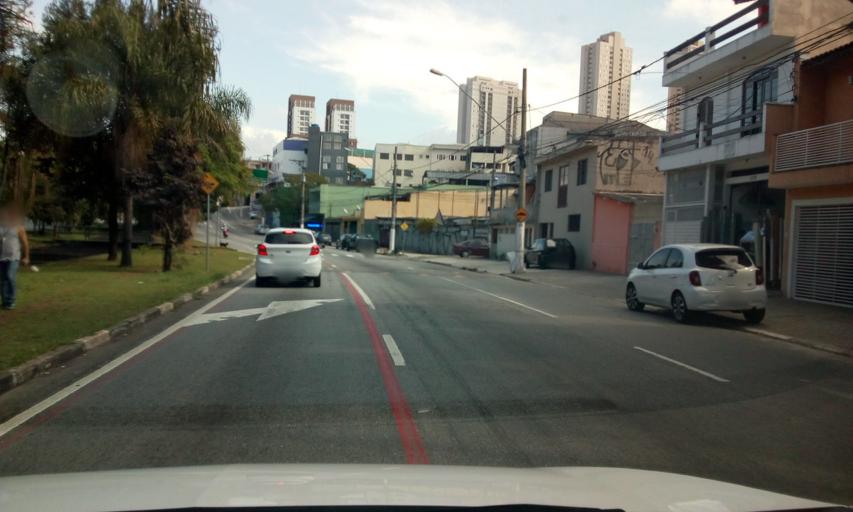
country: BR
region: Sao Paulo
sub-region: Osasco
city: Osasco
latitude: -23.5544
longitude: -46.7806
